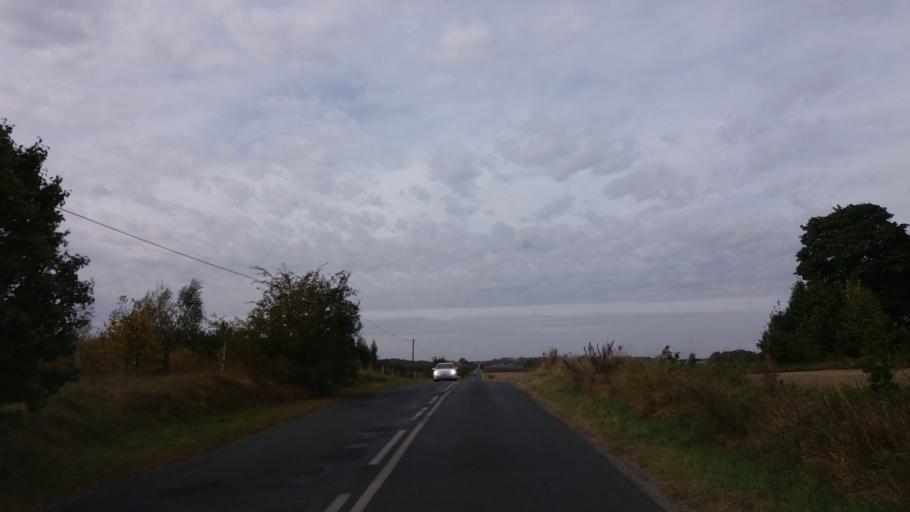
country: PL
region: Lubusz
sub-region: Powiat strzelecko-drezdenecki
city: Strzelce Krajenskie
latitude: 52.9295
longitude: 15.4765
